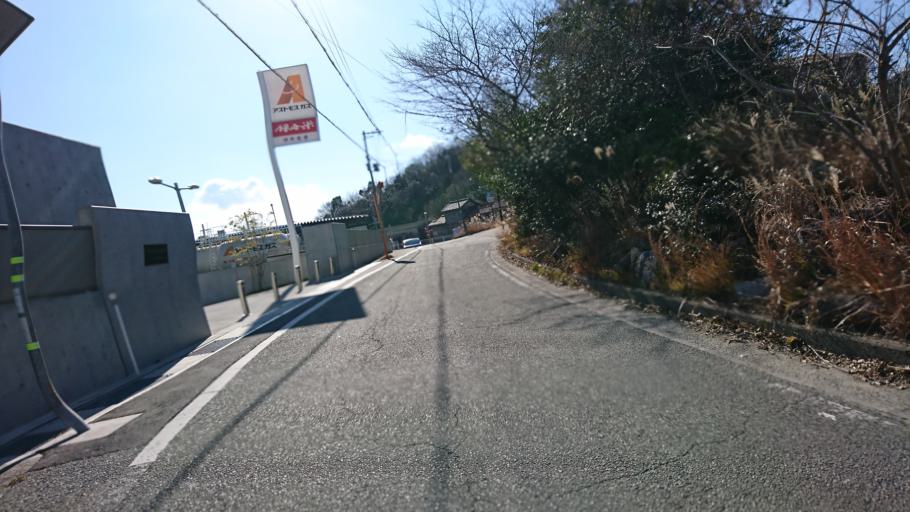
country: JP
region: Hyogo
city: Kakogawacho-honmachi
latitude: 34.7891
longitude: 134.7967
